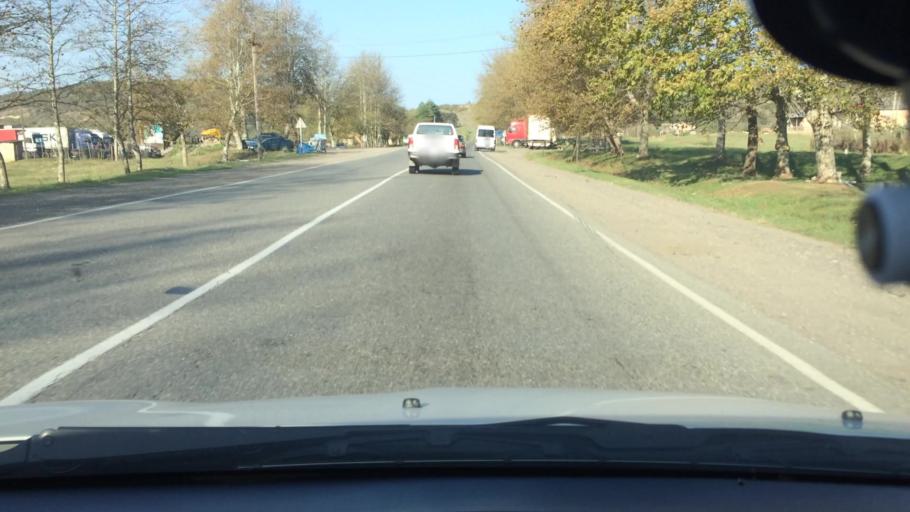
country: GE
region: Imereti
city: Kutaisi
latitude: 42.2146
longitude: 42.8146
